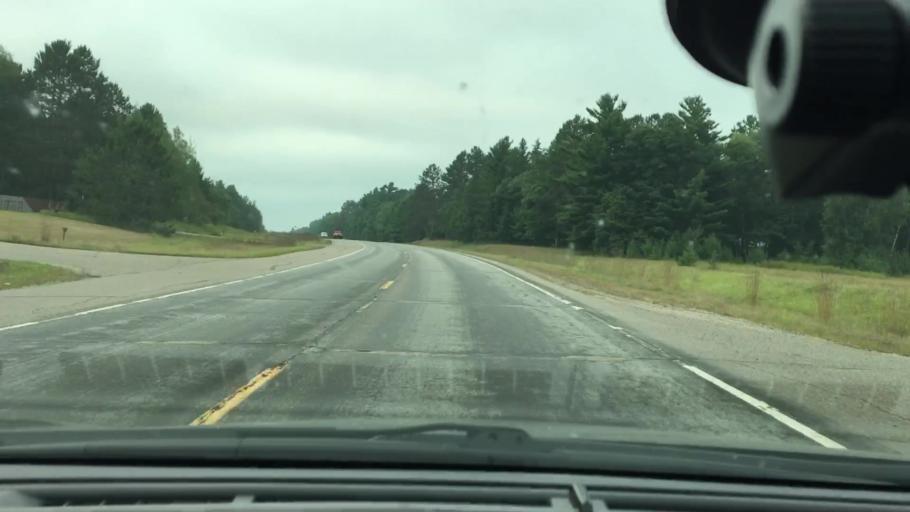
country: US
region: Minnesota
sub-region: Crow Wing County
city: Cross Lake
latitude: 46.7112
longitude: -93.9561
